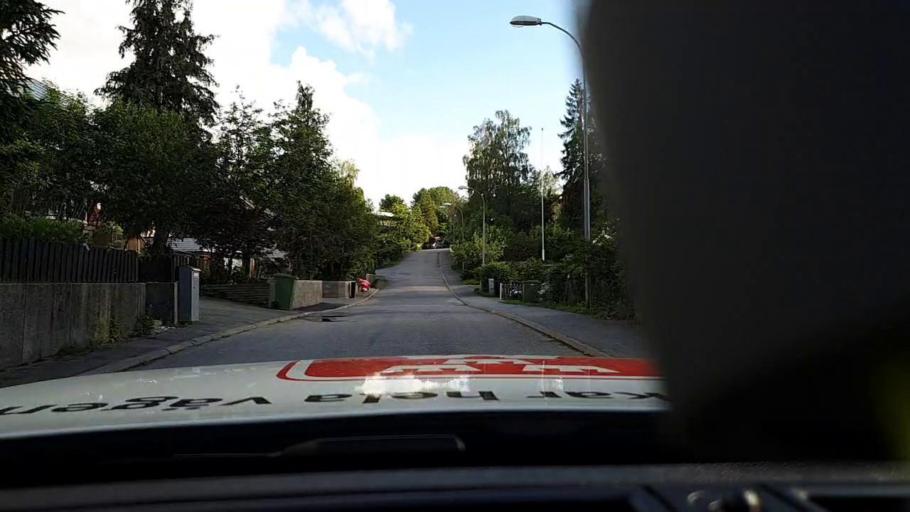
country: SE
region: Stockholm
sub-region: Huddinge Kommun
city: Huddinge
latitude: 59.2481
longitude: 17.9653
